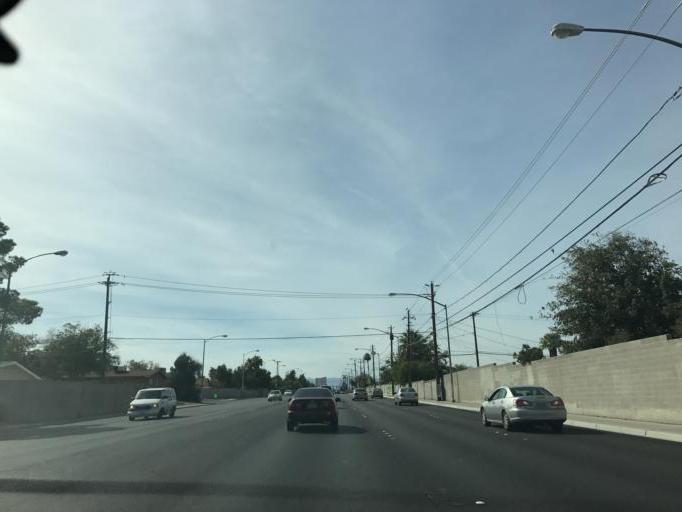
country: US
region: Nevada
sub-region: Clark County
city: Winchester
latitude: 36.1297
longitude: -115.0954
